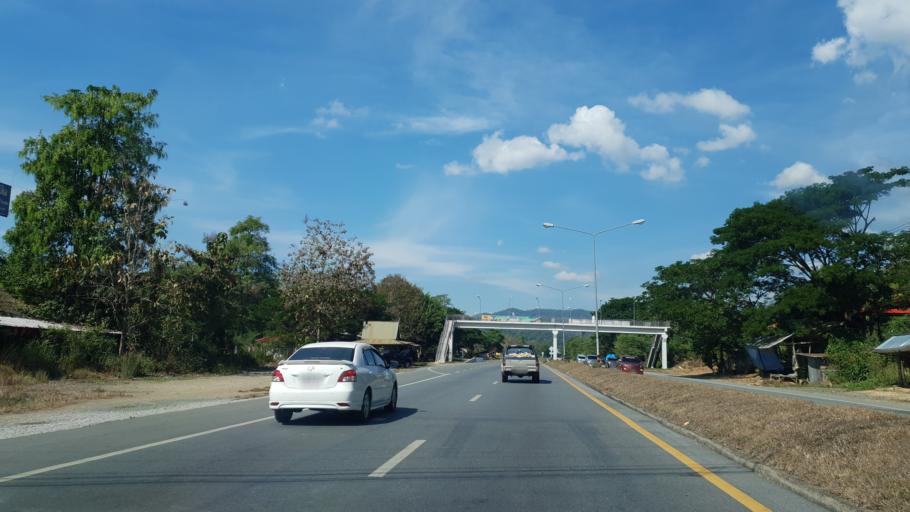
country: TH
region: Uttaradit
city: Lap Lae
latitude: 17.7884
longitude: 100.1177
